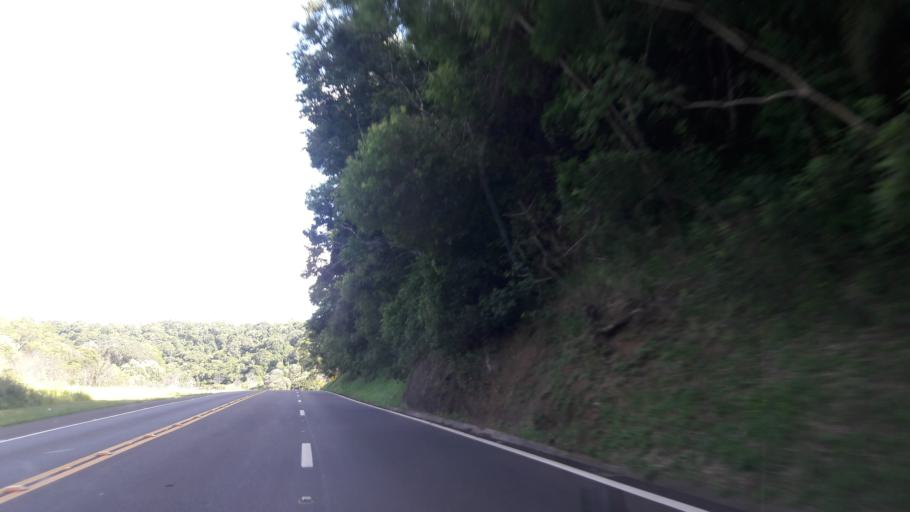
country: BR
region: Parana
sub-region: Laranjeiras Do Sul
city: Laranjeiras do Sul
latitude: -25.4201
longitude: -52.0462
